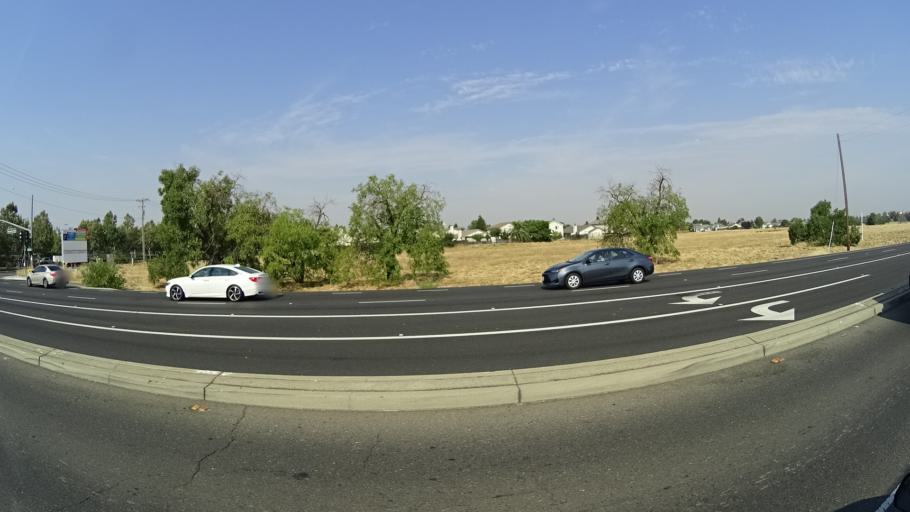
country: US
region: California
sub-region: Sacramento County
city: Laguna
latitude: 38.4310
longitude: -121.4175
